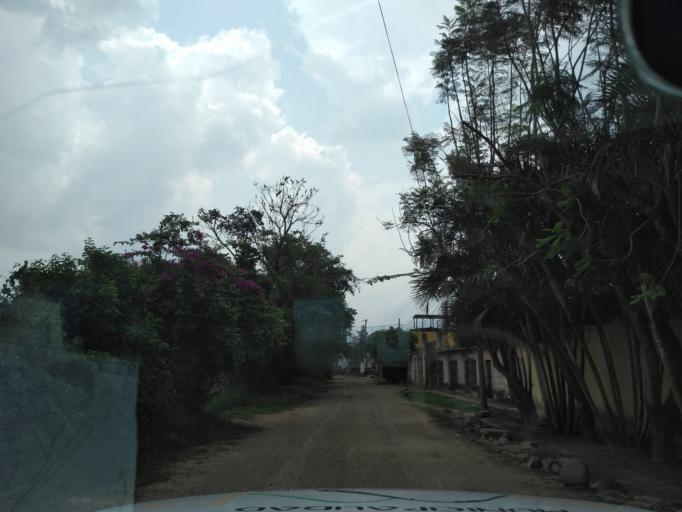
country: GT
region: Guatemala
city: Petapa
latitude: 14.5105
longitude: -90.5547
